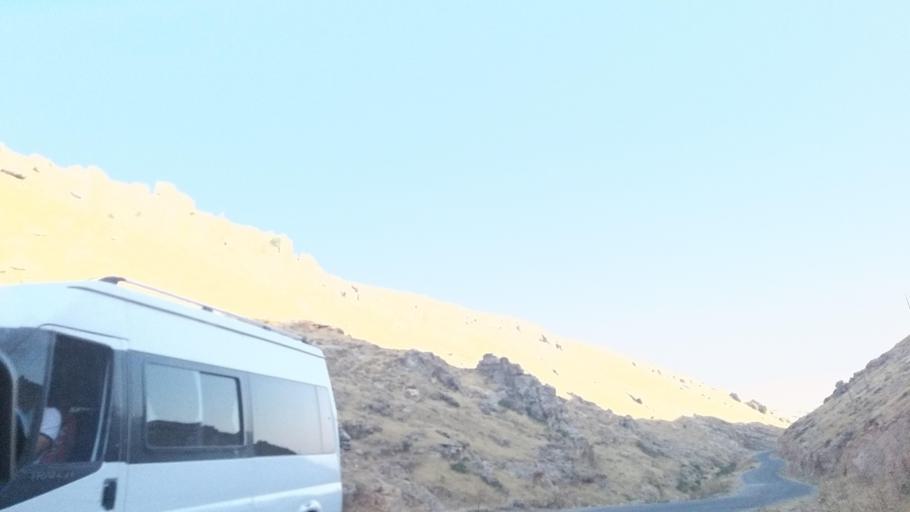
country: TR
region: Diyarbakir
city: Silvan
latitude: 38.1632
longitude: 41.0016
